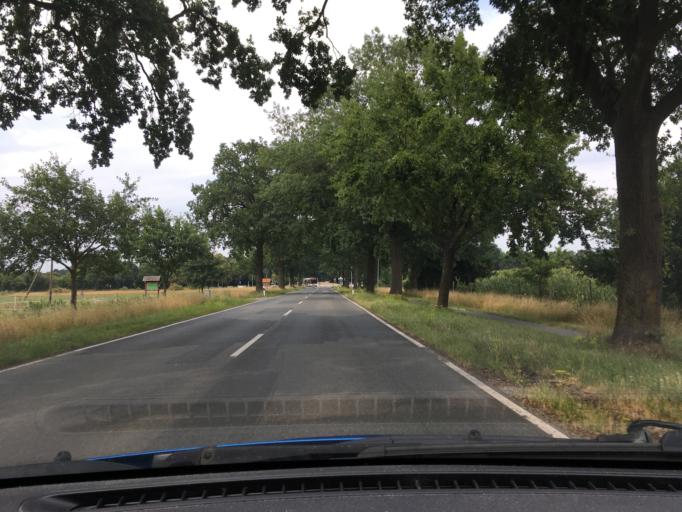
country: DE
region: Lower Saxony
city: Adelheidsdorf
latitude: 52.5675
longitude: 10.0605
